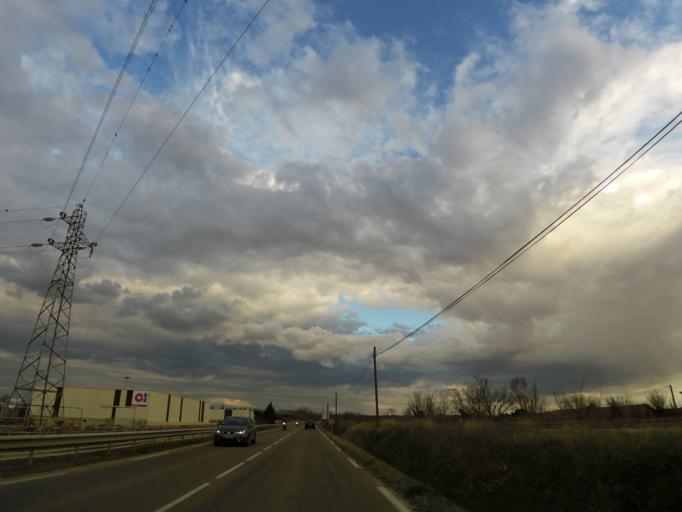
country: FR
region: Languedoc-Roussillon
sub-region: Departement du Gard
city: Vestric-et-Candiac
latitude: 43.7253
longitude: 4.2515
